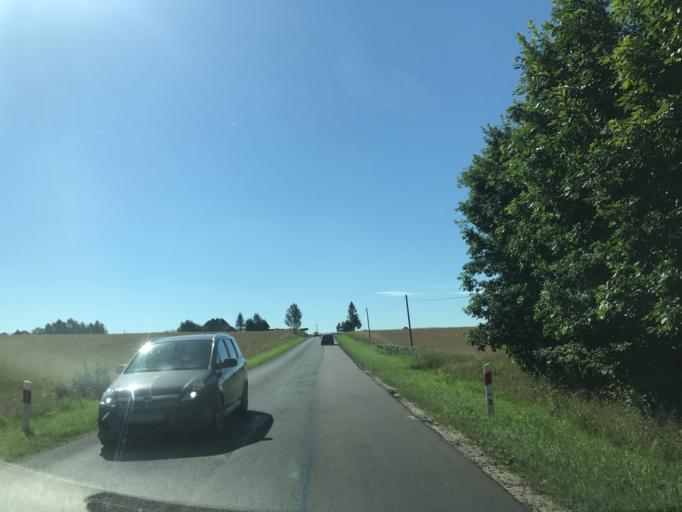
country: PL
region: Pomeranian Voivodeship
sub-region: Powiat bytowski
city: Czarna Dabrowka
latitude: 54.3692
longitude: 17.5026
